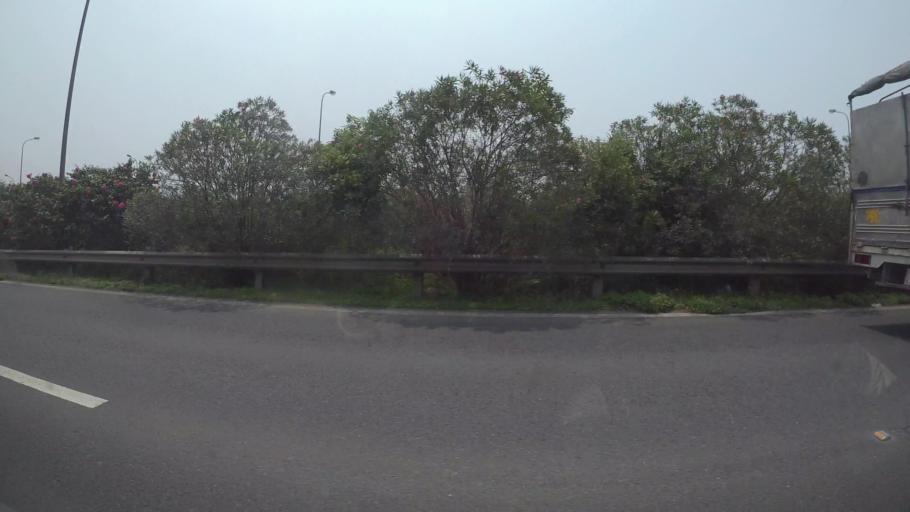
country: VN
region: Ha Noi
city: Quoc Oai
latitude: 20.9980
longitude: 105.5950
